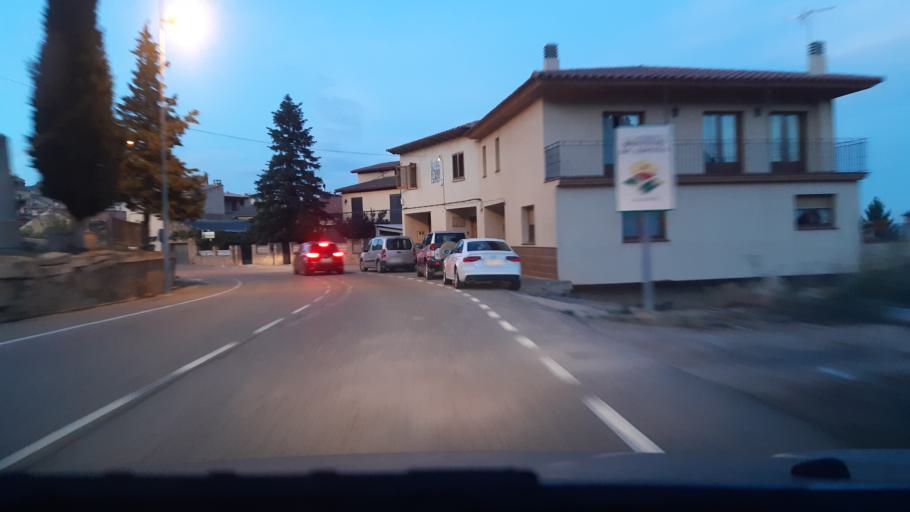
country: ES
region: Aragon
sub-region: Provincia de Teruel
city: Calaceite
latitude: 41.0129
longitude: 0.1870
